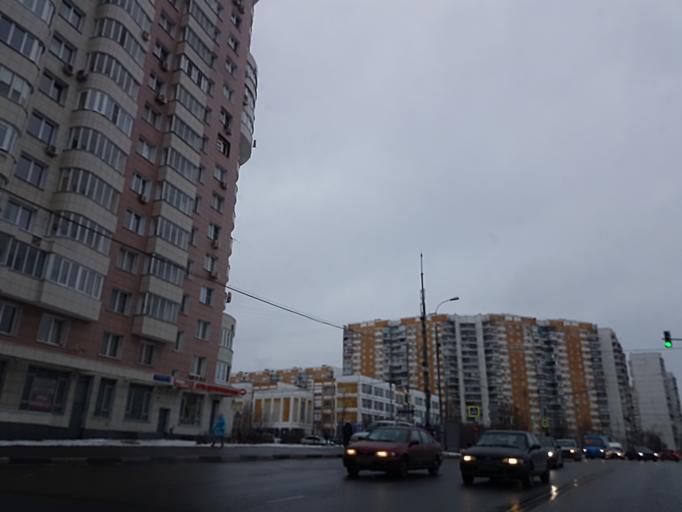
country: RU
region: Moskovskaya
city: Pavshino
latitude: 55.8309
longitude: 37.3546
